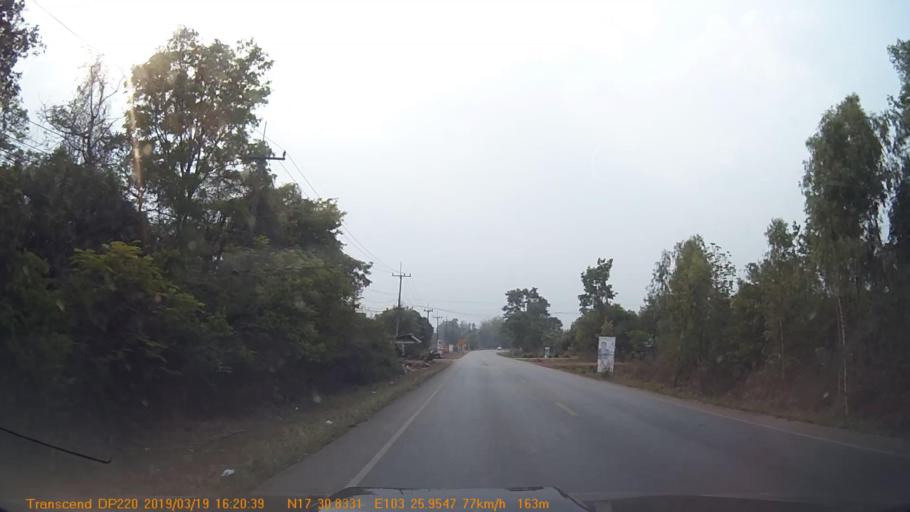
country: TH
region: Sakon Nakhon
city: Sawang Daen Din
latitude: 17.5143
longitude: 103.4320
